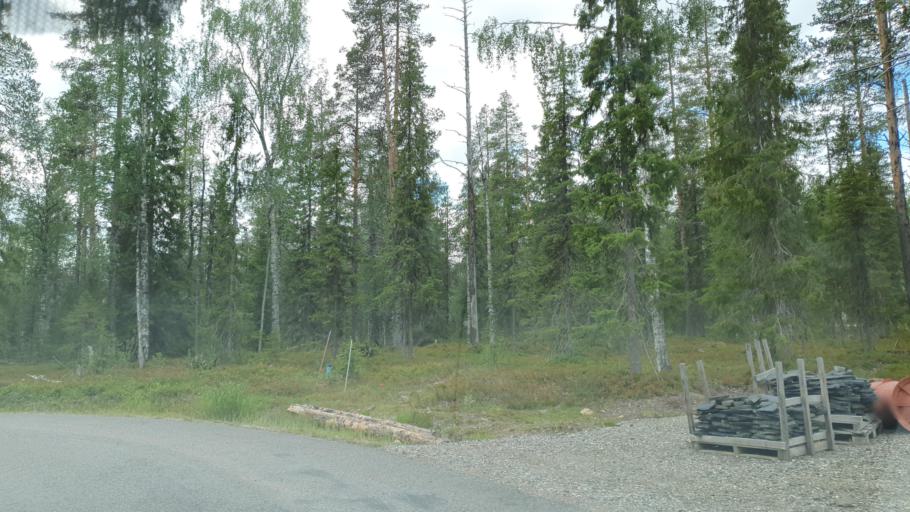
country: FI
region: Lapland
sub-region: Tunturi-Lappi
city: Kolari
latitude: 67.5511
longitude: 24.2767
